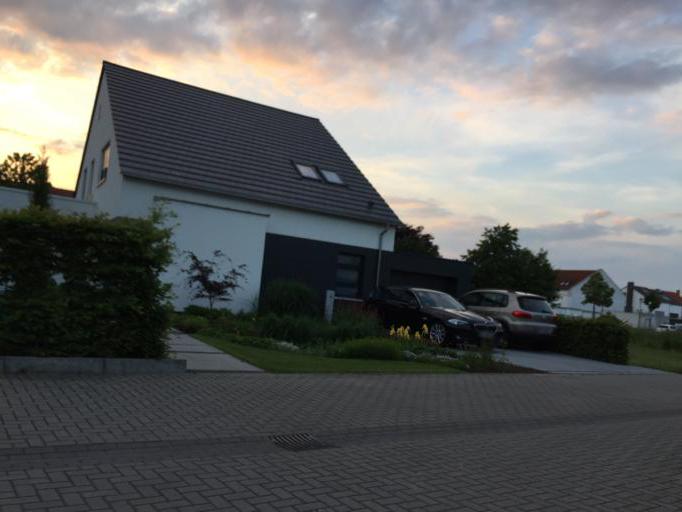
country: DE
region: Baden-Wuerttemberg
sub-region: Karlsruhe Region
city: Schwetzingen
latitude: 49.3739
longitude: 8.5682
